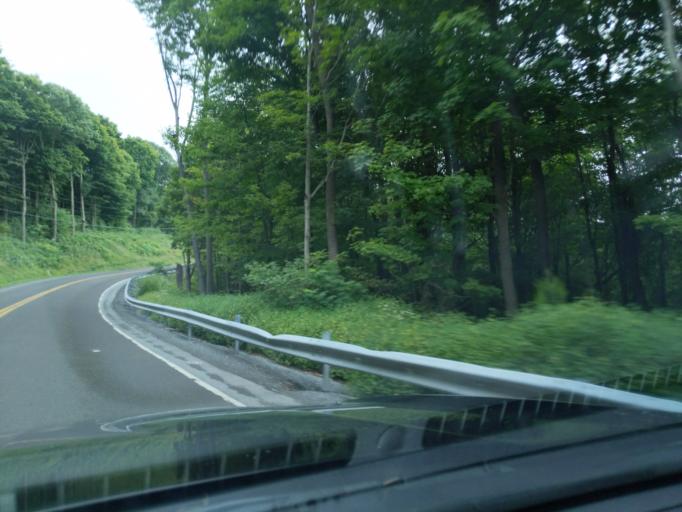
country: US
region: Pennsylvania
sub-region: Blair County
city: Claysburg
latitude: 40.3553
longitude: -78.5176
